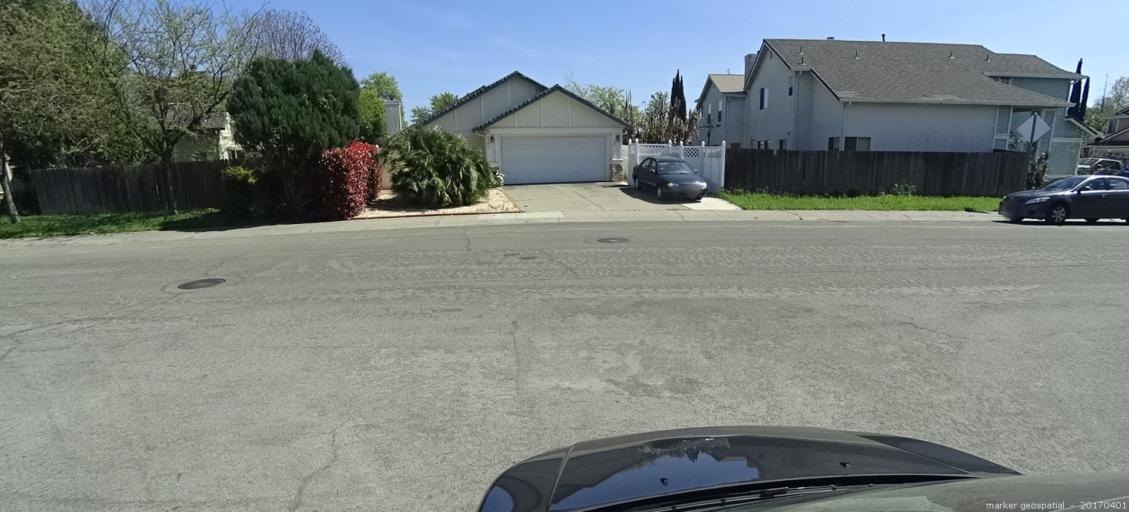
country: US
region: California
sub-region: Sacramento County
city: Laguna
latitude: 38.4461
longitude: -121.4305
